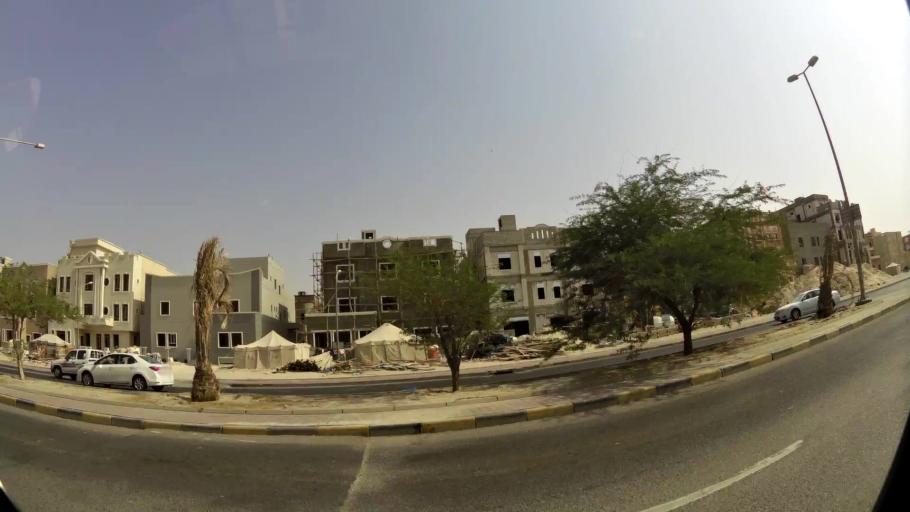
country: KW
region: Muhafazat al Jahra'
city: Al Jahra'
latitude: 29.3211
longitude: 47.6790
